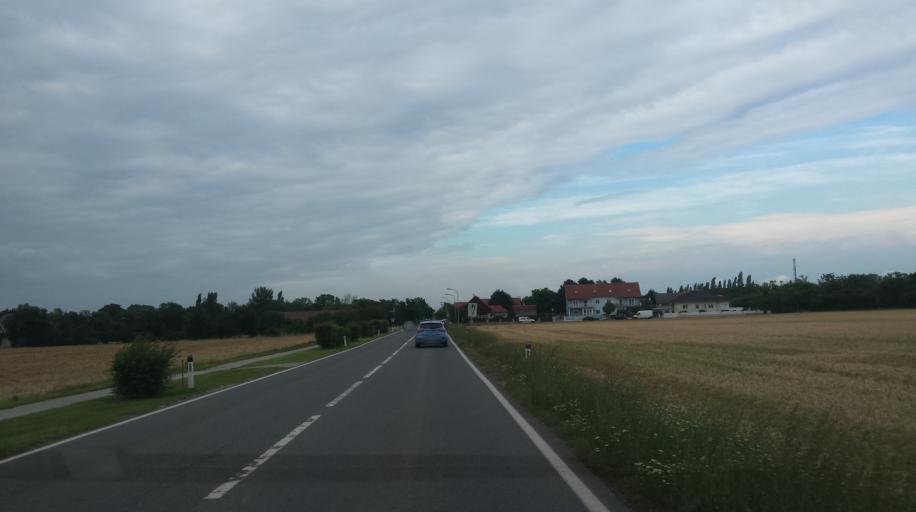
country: AT
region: Lower Austria
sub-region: Politischer Bezirk Wien-Umgebung
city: Zwolfaxing
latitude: 48.1028
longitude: 16.4579
